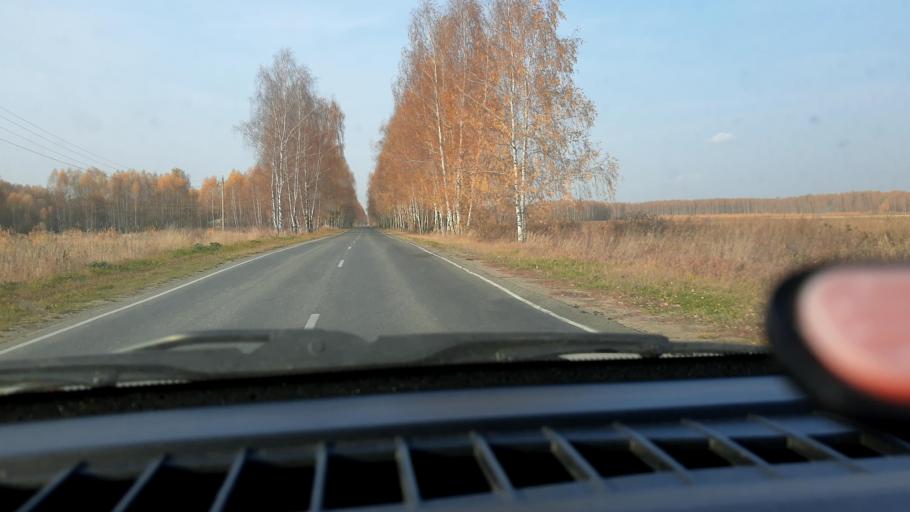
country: RU
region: Nizjnij Novgorod
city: Neklyudovo
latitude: 56.4791
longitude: 43.8724
